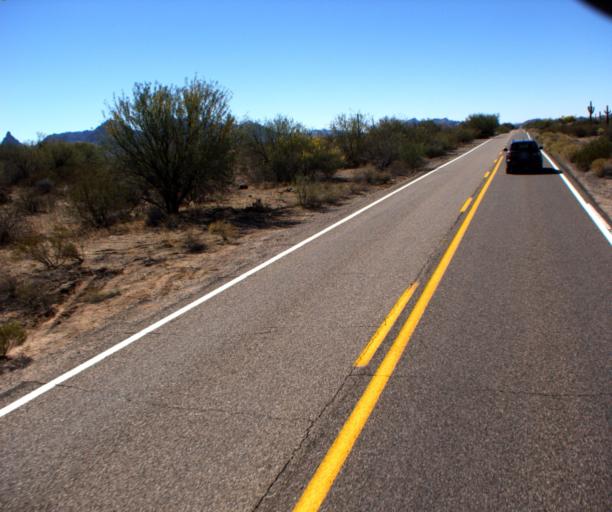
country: US
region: Arizona
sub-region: Pima County
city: Ajo
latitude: 32.1728
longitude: -112.7627
